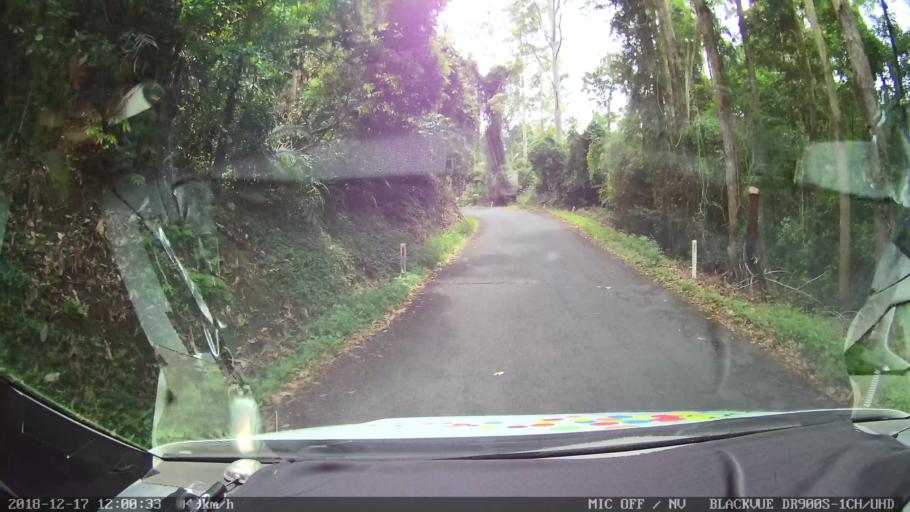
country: AU
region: New South Wales
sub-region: Kyogle
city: Kyogle
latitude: -28.5249
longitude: 152.5686
